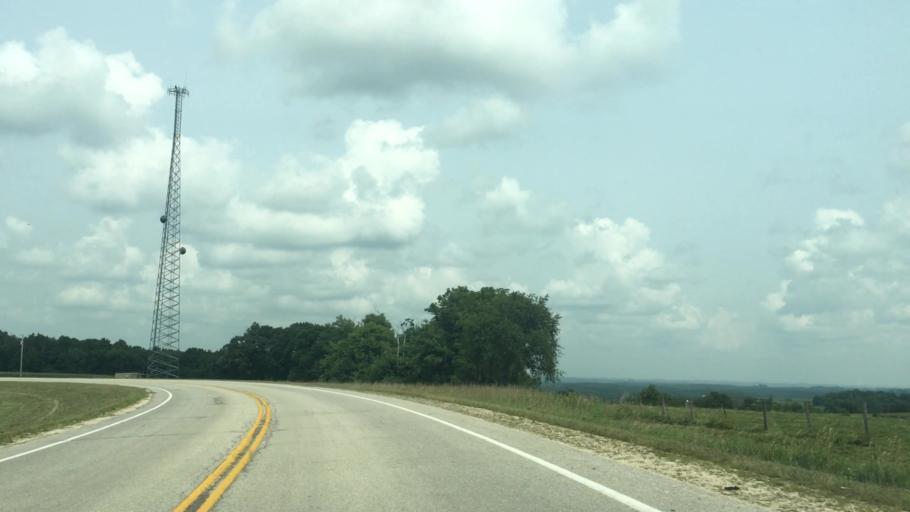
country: US
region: Minnesota
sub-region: Fillmore County
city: Harmony
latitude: 43.6642
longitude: -91.9302
